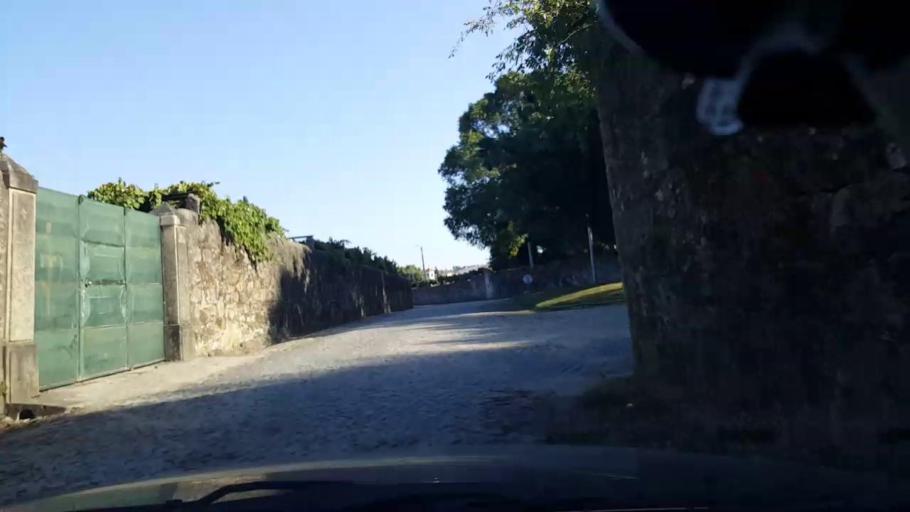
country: PT
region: Porto
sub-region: Vila do Conde
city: Arvore
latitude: 41.3405
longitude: -8.6849
